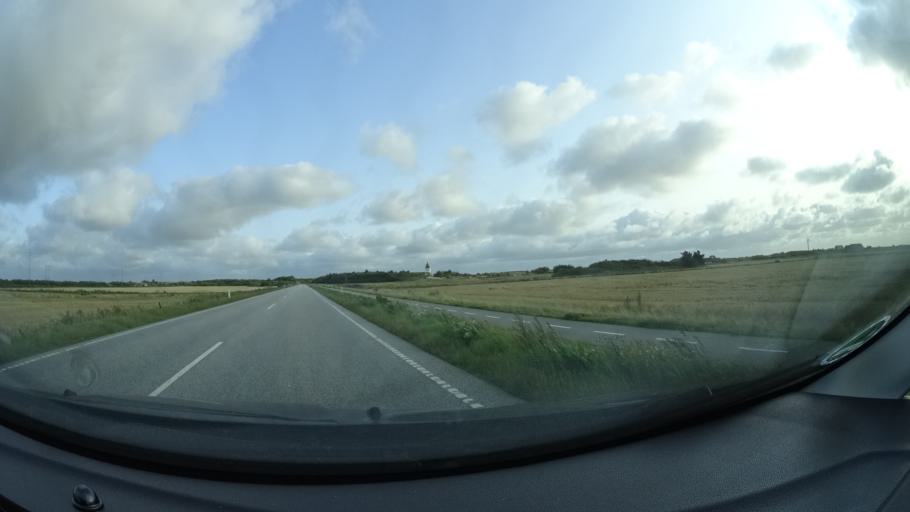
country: DK
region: Central Jutland
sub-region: Lemvig Kommune
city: Harboore
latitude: 56.6266
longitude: 8.1854
